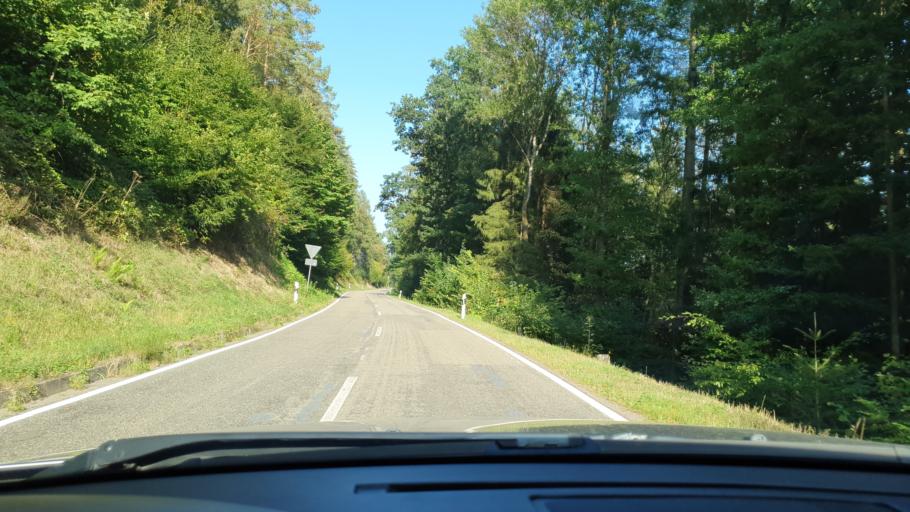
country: DE
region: Rheinland-Pfalz
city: Hohfroschen
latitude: 49.2745
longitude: 7.5581
